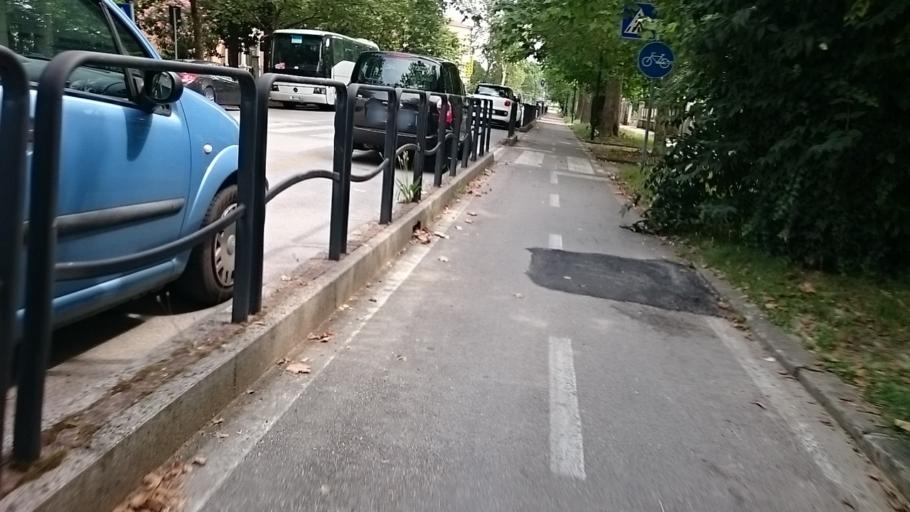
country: IT
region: Veneto
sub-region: Provincia di Venezia
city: Mestre
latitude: 45.4778
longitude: 12.2270
